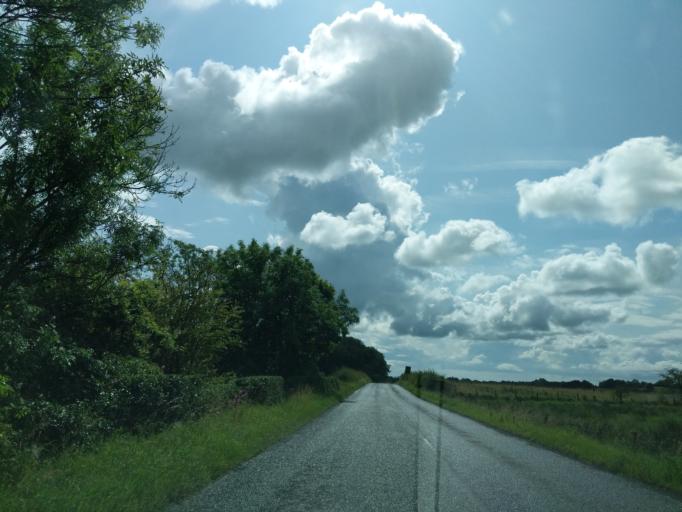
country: GB
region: Scotland
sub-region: East Ayrshire
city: Stewarton
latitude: 55.7170
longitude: -4.5103
